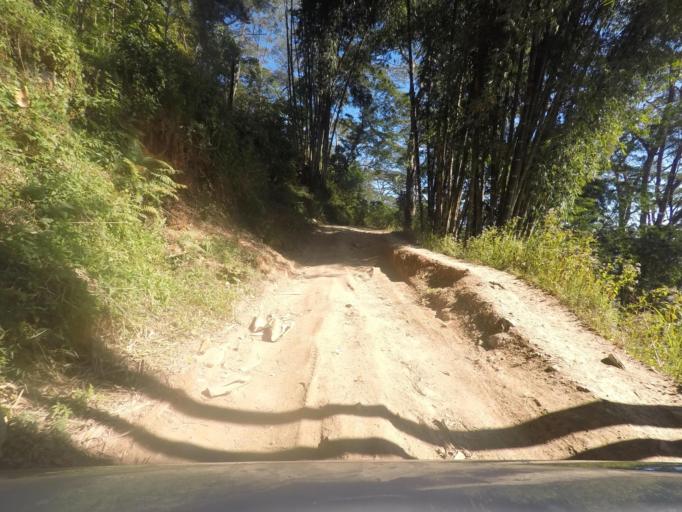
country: TL
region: Ermera
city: Gleno
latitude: -8.7430
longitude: 125.3486
